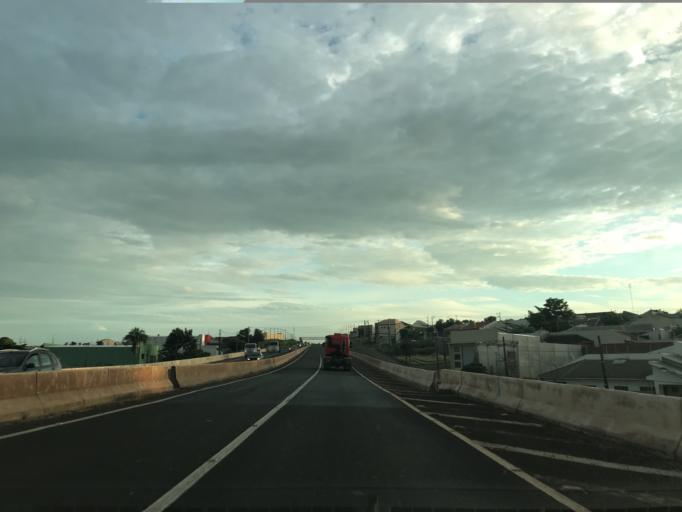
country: BR
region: Parana
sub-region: Maringa
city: Maringa
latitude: -23.3874
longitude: -51.9667
